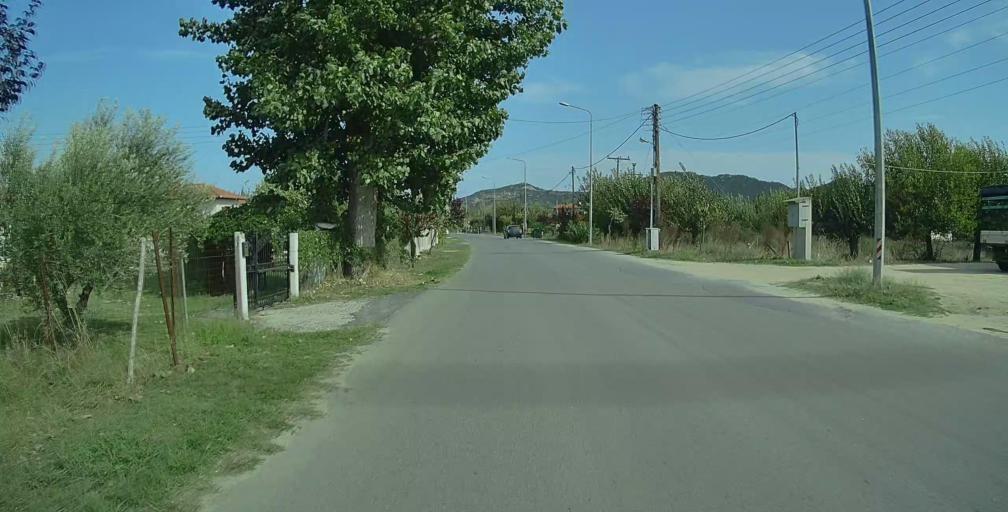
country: GR
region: Central Macedonia
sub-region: Nomos Chalkidikis
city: Sykia
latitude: 40.0363
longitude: 23.9522
